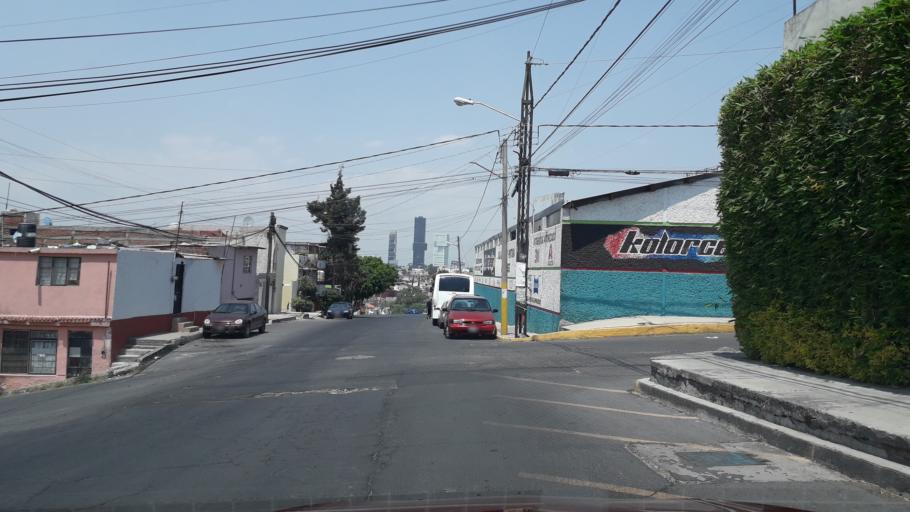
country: MX
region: Puebla
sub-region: San Pedro Cholula
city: Santiago Momoxpan
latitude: 19.0539
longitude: -98.2368
